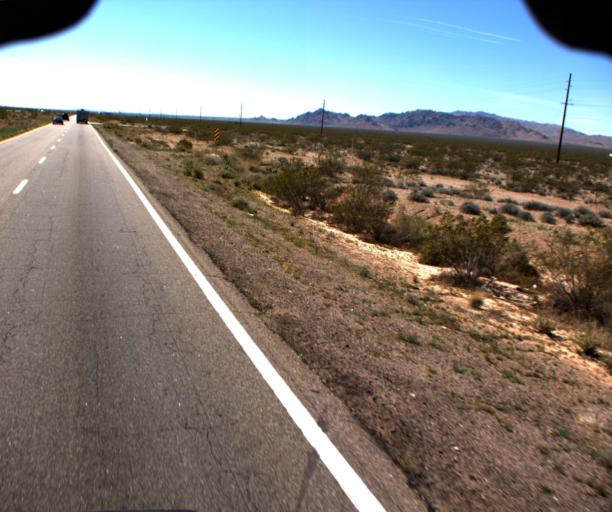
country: US
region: Arizona
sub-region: Mohave County
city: Dolan Springs
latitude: 35.6993
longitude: -114.4745
